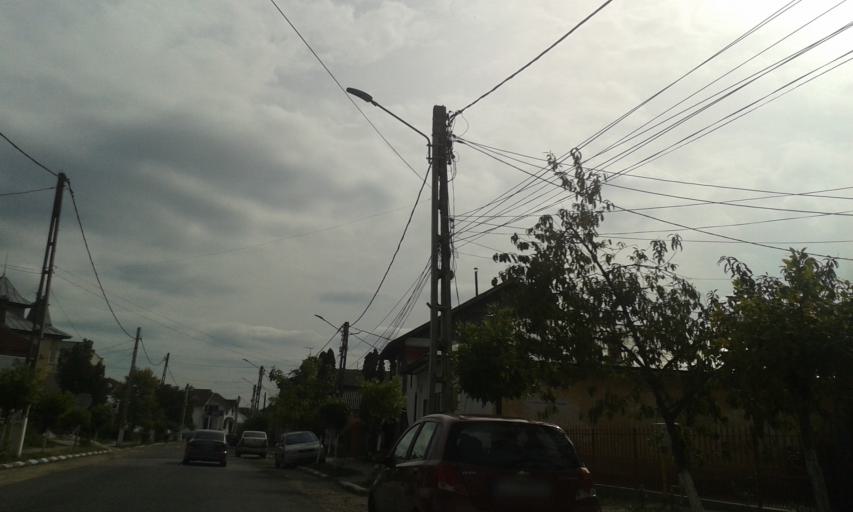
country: RO
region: Gorj
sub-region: Comuna Targu Carbunesti
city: Targu Carbunesti
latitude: 44.9567
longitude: 23.5125
